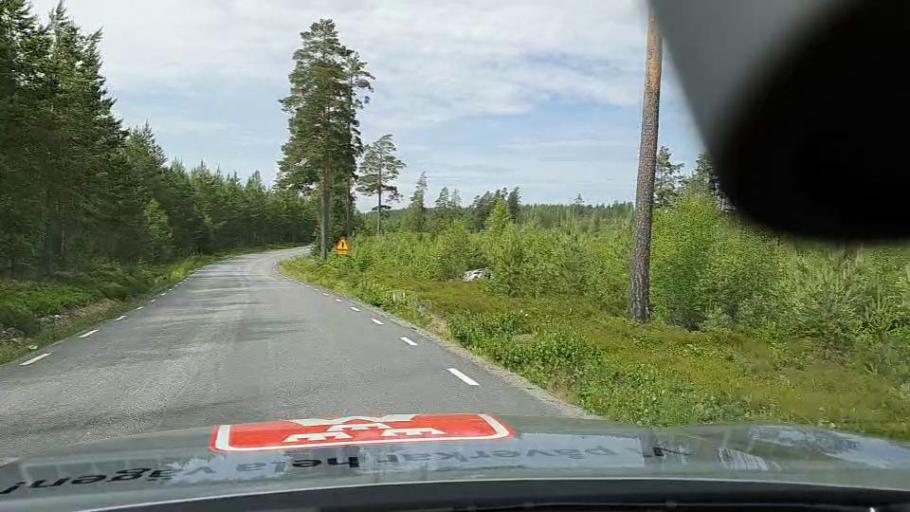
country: SE
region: Soedermanland
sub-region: Eskilstuna Kommun
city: Arla
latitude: 59.2421
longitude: 16.7201
